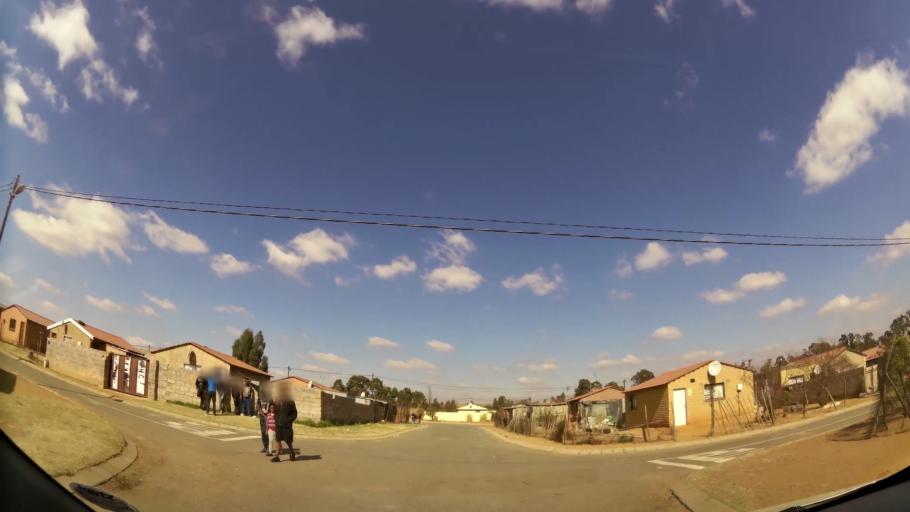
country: ZA
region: Gauteng
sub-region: West Rand District Municipality
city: Krugersdorp
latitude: -26.1458
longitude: 27.7821
